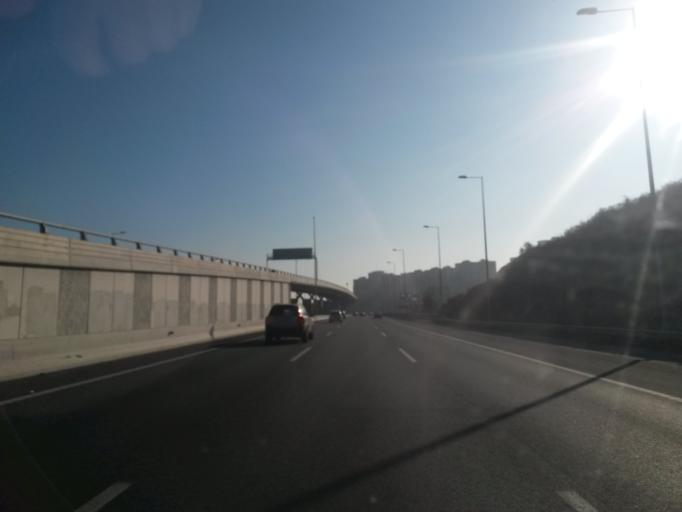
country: ES
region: Catalonia
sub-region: Provincia de Barcelona
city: Montcada i Reixac
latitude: 41.4670
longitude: 2.1725
